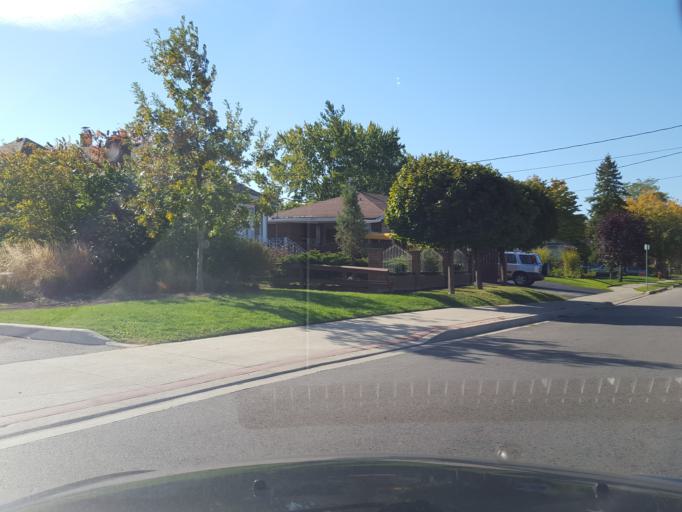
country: CA
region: Ontario
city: Burlington
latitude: 43.3386
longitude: -79.8193
